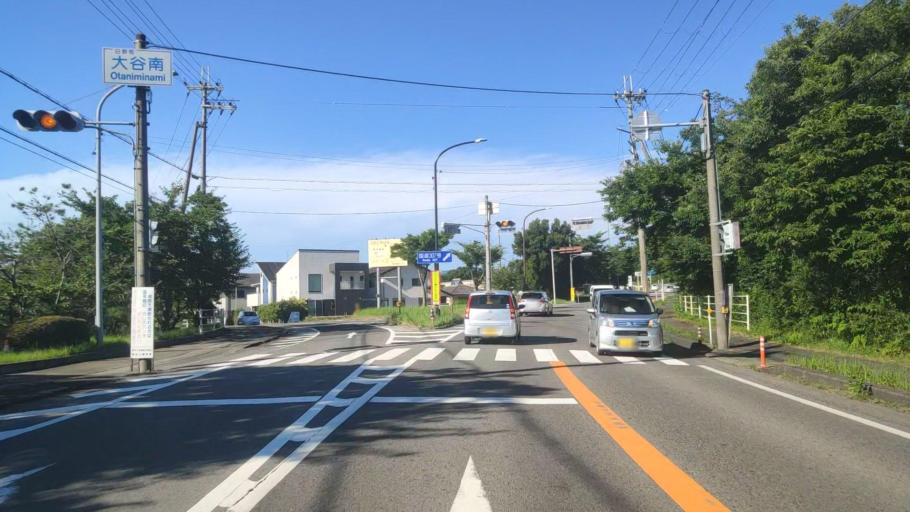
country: JP
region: Shiga Prefecture
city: Hino
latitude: 35.0285
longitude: 136.2402
